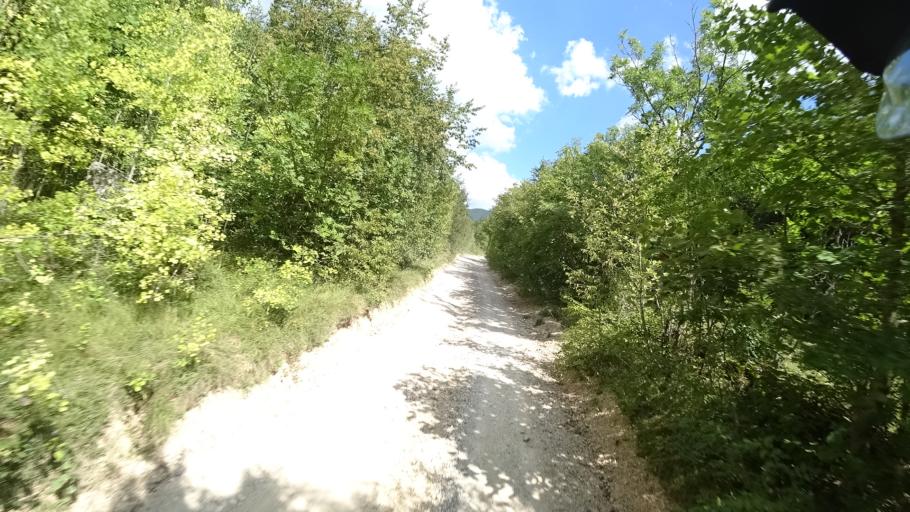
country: HR
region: Zadarska
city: Gracac
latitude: 44.5568
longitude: 15.8265
